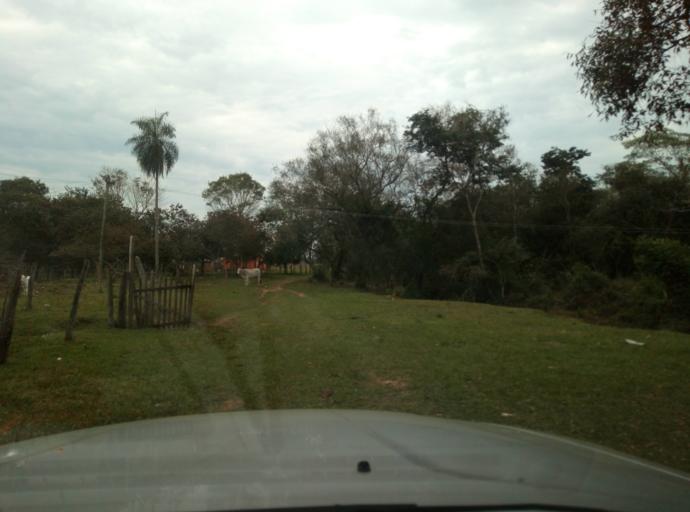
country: PY
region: Caaguazu
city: Carayao
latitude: -25.1628
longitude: -56.3333
